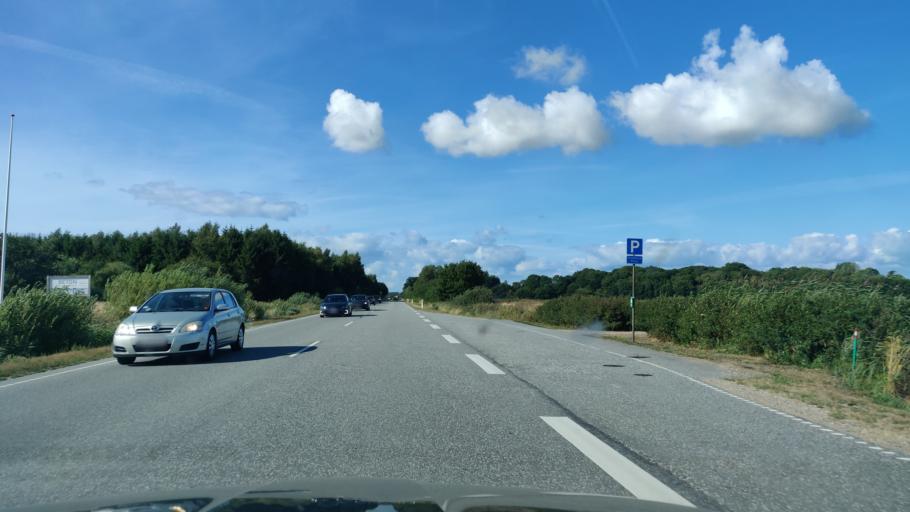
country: DK
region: Zealand
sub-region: Odsherred Kommune
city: Hojby
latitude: 55.8891
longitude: 11.5688
